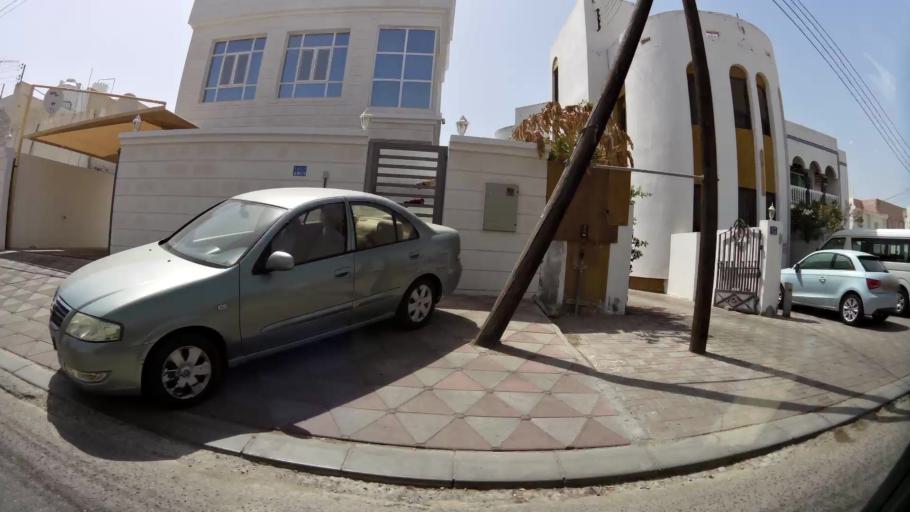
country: OM
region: Muhafazat Masqat
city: Bawshar
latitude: 23.5917
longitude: 58.4231
